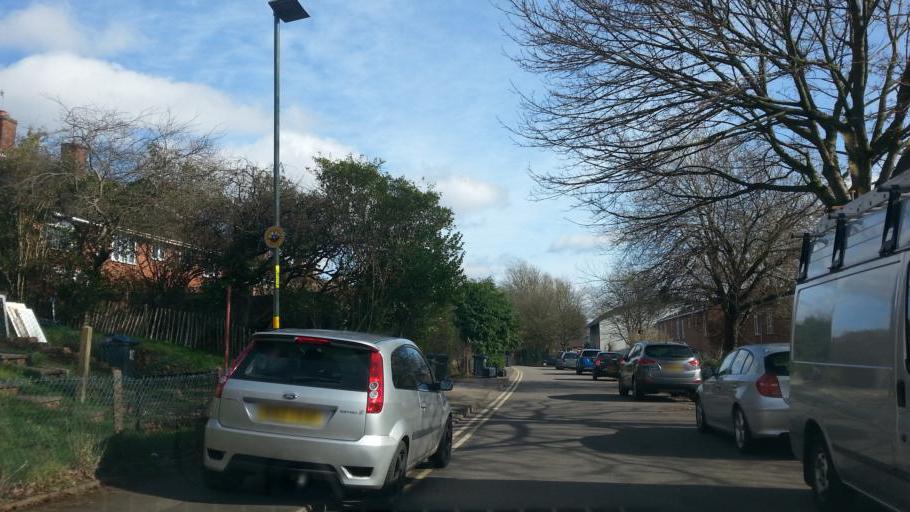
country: GB
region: England
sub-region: City and Borough of Birmingham
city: Bartley Green
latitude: 52.4472
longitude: -1.9555
